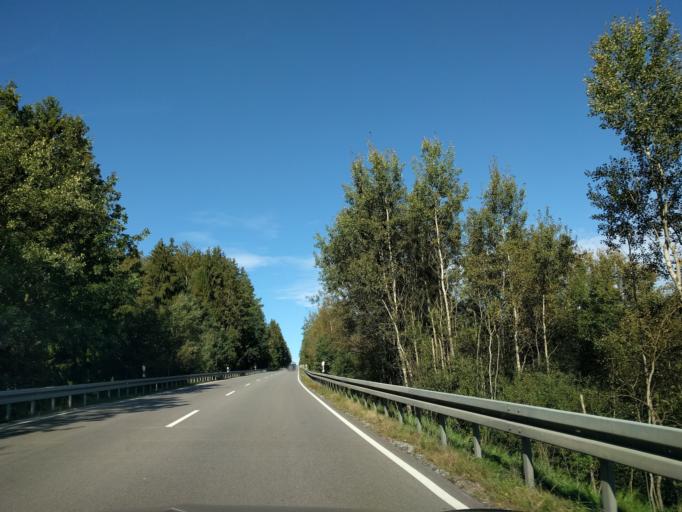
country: DE
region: Bavaria
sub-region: Lower Bavaria
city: Viechtach
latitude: 49.0574
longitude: 12.9116
